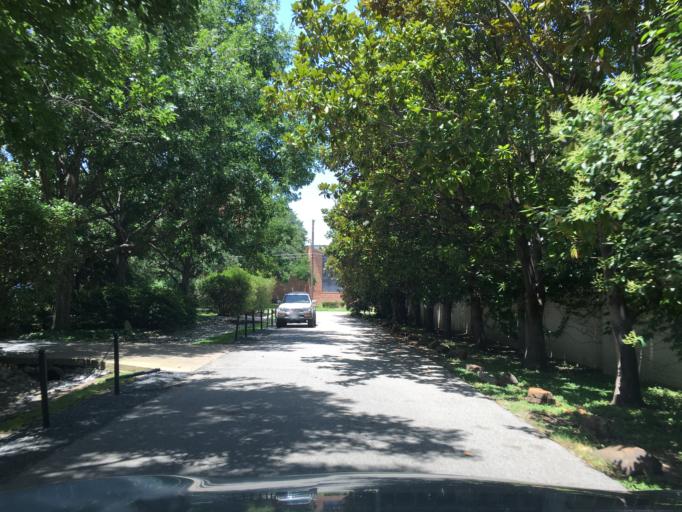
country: US
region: Texas
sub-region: Dallas County
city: University Park
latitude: 32.8771
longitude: -96.8077
